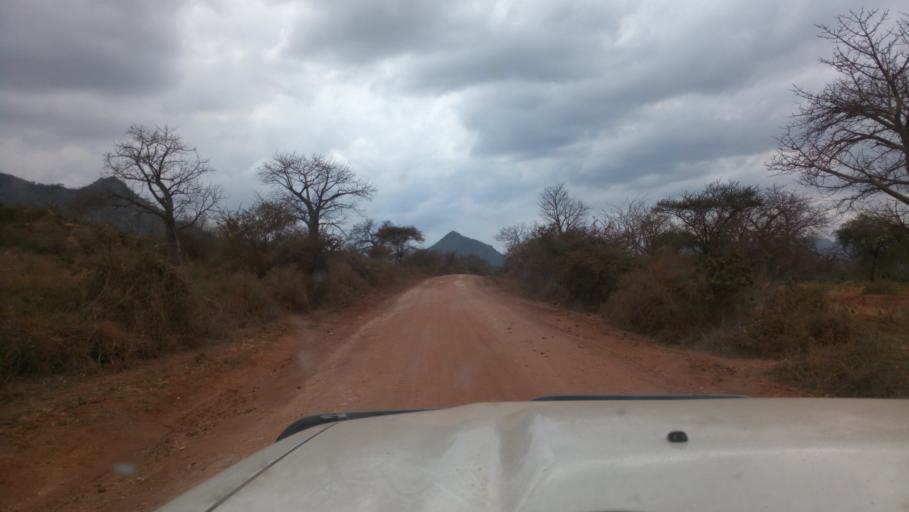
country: KE
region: Kitui
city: Kitui
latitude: -1.8758
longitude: 38.4312
